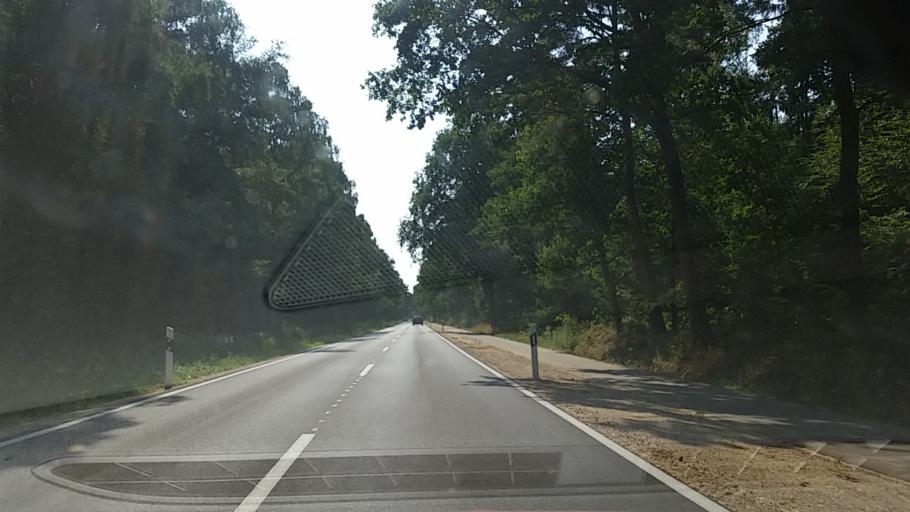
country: DE
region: Schleswig-Holstein
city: Wohltorf
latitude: 53.5580
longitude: 10.2765
